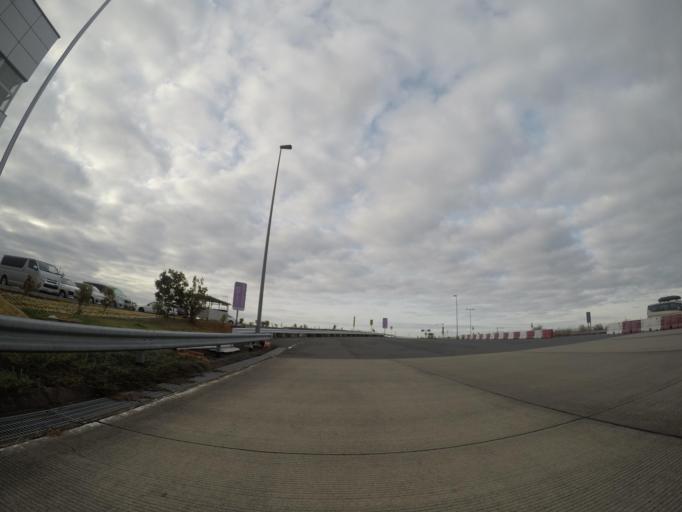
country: JP
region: Shizuoka
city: Hamakita
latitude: 34.8317
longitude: 137.8140
